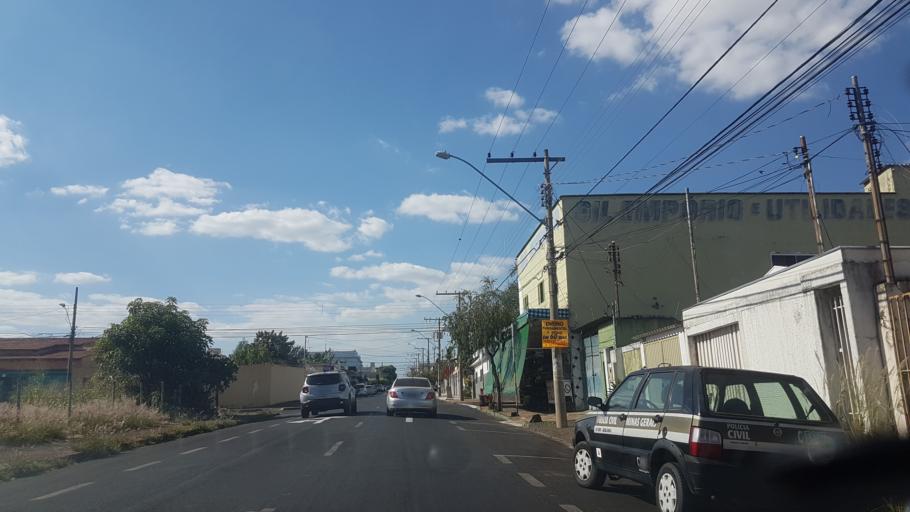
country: BR
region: Minas Gerais
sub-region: Uberlandia
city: Uberlandia
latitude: -18.8953
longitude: -48.2675
